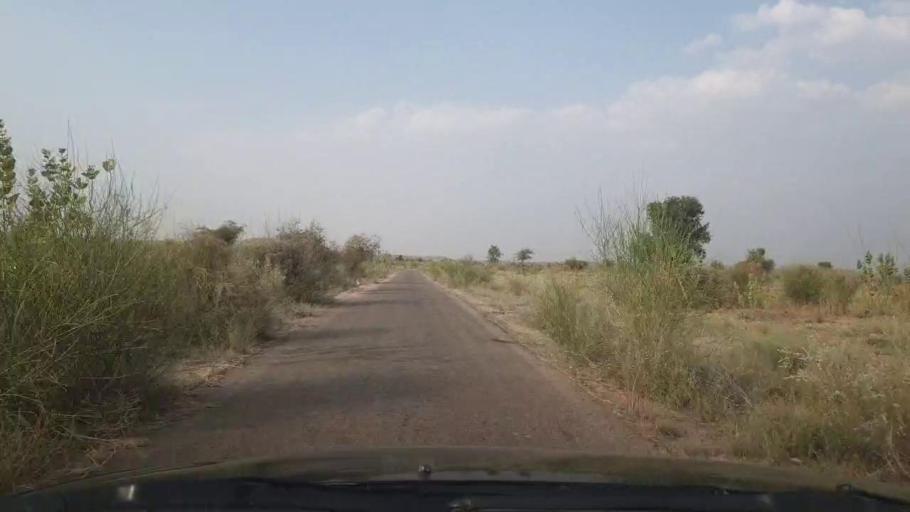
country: PK
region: Sindh
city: Islamkot
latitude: 25.0570
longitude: 70.5603
